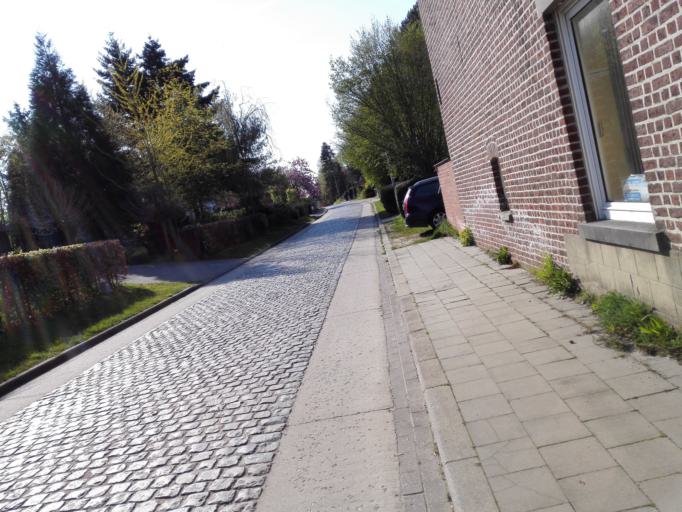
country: BE
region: Flanders
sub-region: Provincie Vlaams-Brabant
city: Leuven
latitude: 50.8729
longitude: 4.7430
